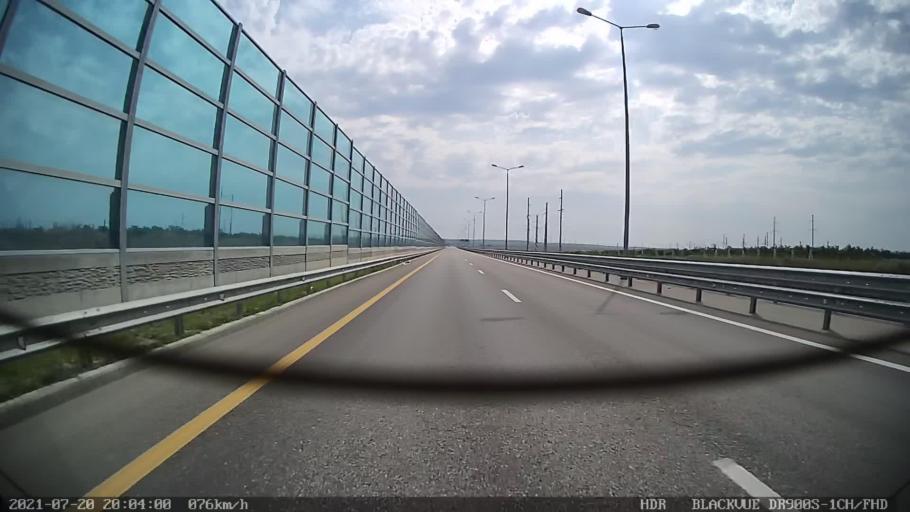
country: RU
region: Krasnodarskiy
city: Taman'
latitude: 45.1864
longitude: 36.6826
